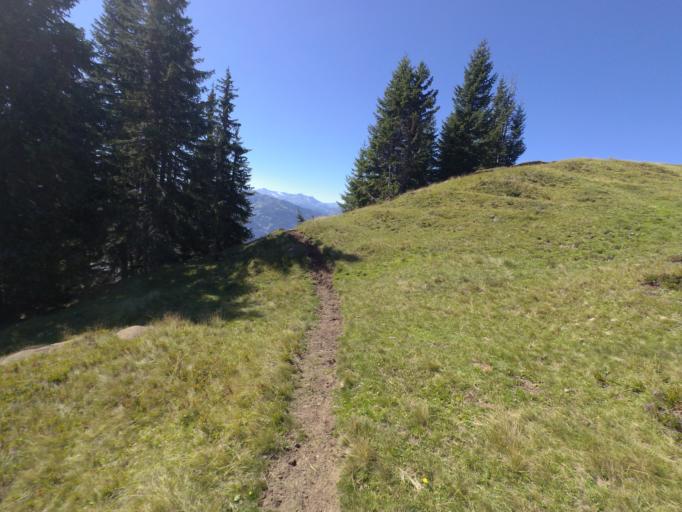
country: AT
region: Salzburg
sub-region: Politischer Bezirk Sankt Johann im Pongau
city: Goldegg
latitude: 47.3490
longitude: 13.0685
